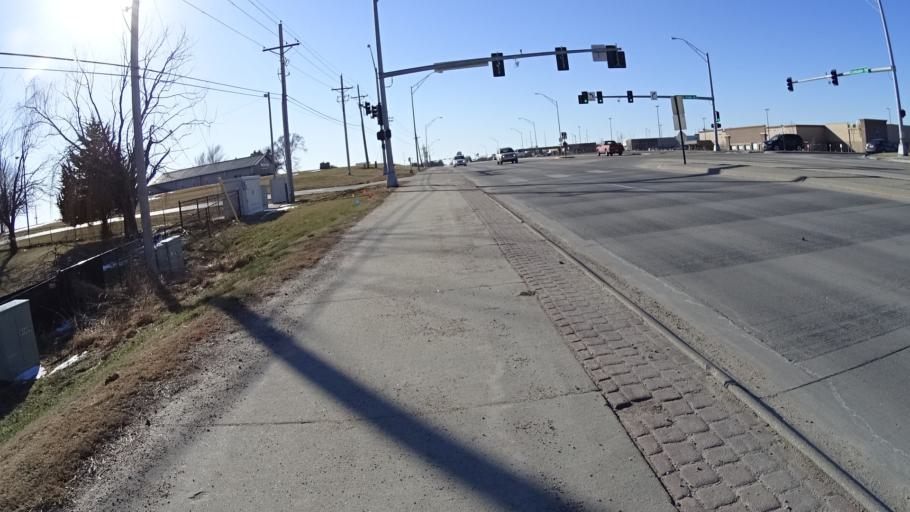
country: US
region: Nebraska
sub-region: Sarpy County
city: Papillion
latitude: 41.1616
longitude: -96.0186
